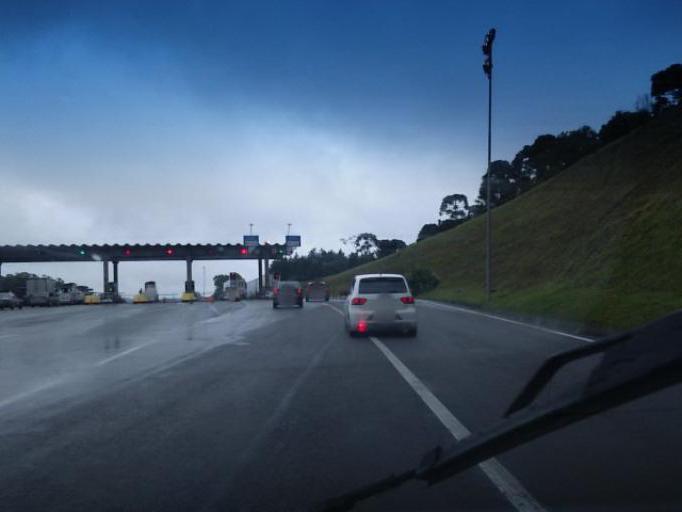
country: BR
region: Parana
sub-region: Sao Jose Dos Pinhais
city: Sao Jose dos Pinhais
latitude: -25.7482
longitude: -49.1288
